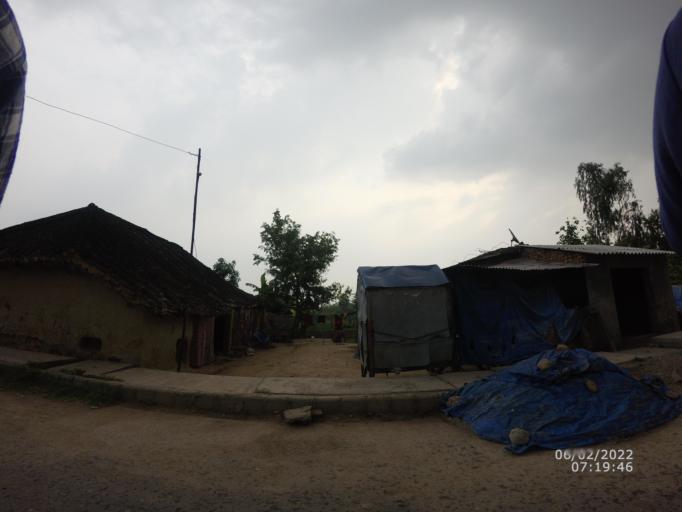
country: NP
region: Western Region
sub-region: Lumbini Zone
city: Bhairahawa
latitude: 27.4846
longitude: 83.4402
